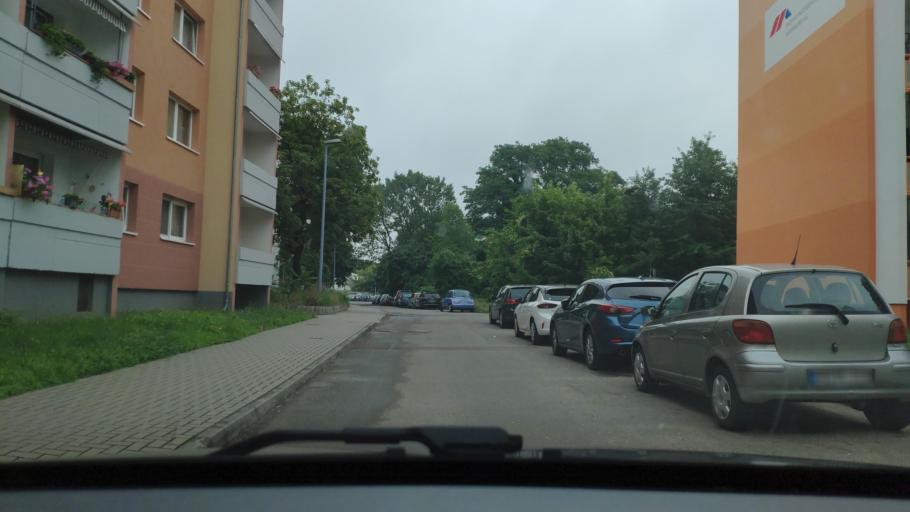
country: DE
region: Saxony-Anhalt
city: Bernburg
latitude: 51.7998
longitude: 11.7384
